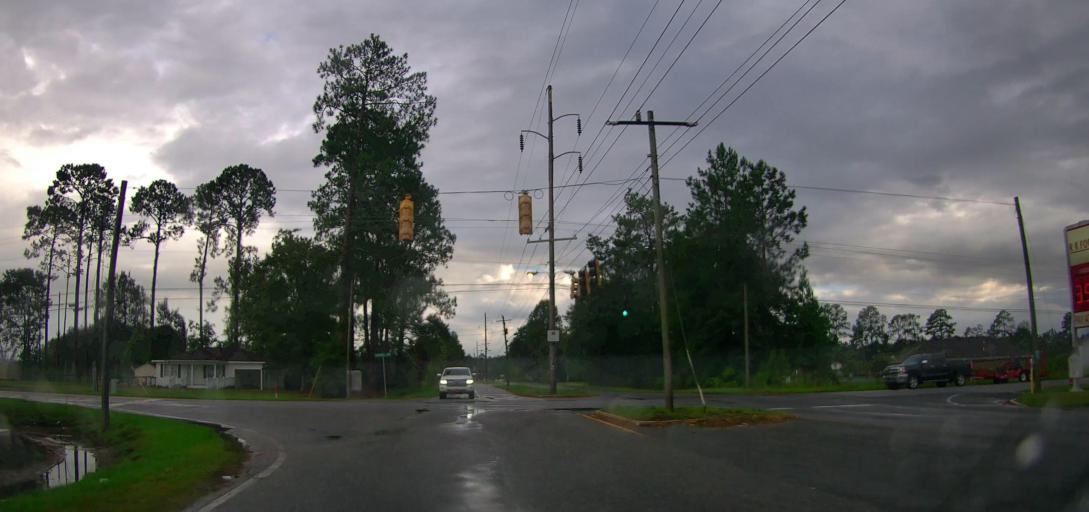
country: US
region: Georgia
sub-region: Ware County
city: Deenwood
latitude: 31.2142
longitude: -82.3883
